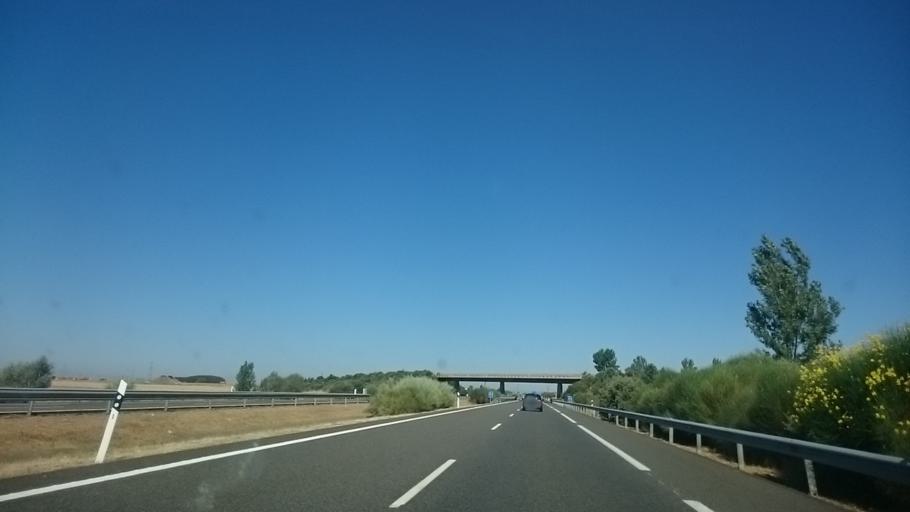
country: ES
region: Castille and Leon
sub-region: Provincia de Leon
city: Santas Martas
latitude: 42.4375
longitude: -5.3454
